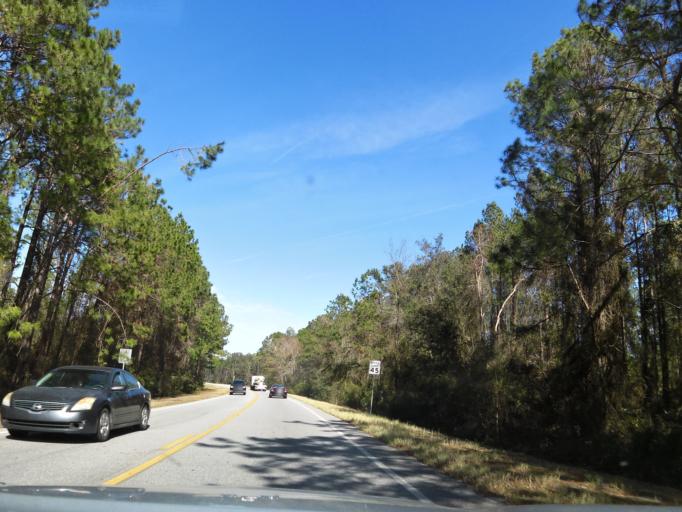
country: US
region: Georgia
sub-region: Glynn County
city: Country Club Estates
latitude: 31.2978
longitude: -81.4854
